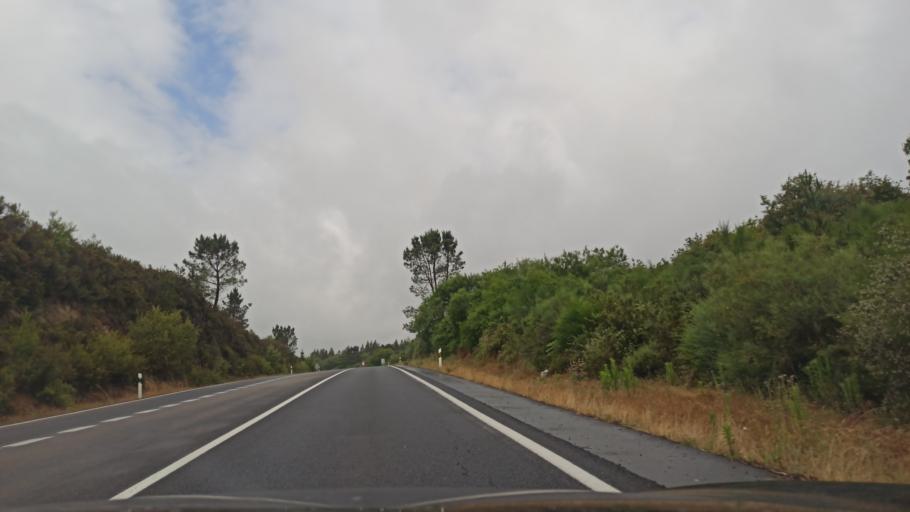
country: ES
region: Galicia
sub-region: Provincia de Pontevedra
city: Rodeiro
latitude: 42.7718
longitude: -7.9645
